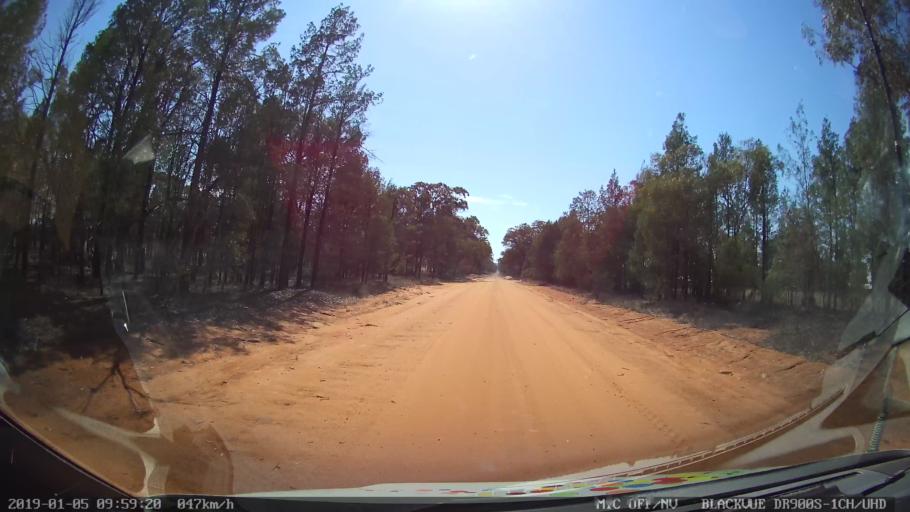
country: AU
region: New South Wales
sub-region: Gilgandra
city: Gilgandra
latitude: -31.6674
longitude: 148.8172
